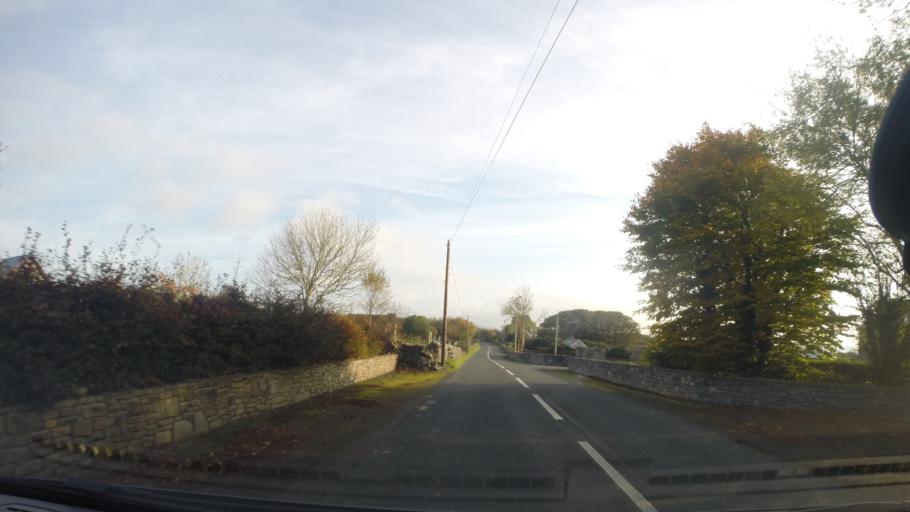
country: IE
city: Ballisodare
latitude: 54.2489
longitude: -8.5265
